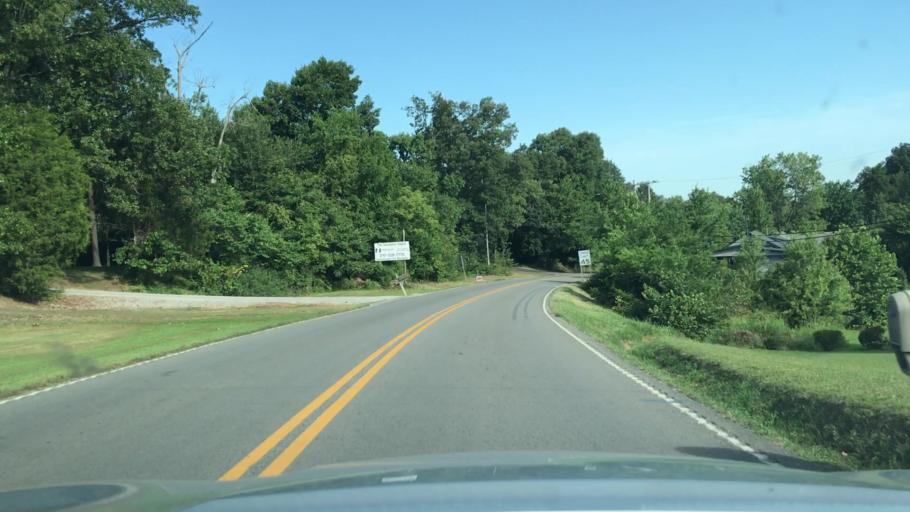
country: US
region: Kentucky
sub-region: Muhlenberg County
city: Greenville
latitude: 37.1898
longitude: -87.1710
